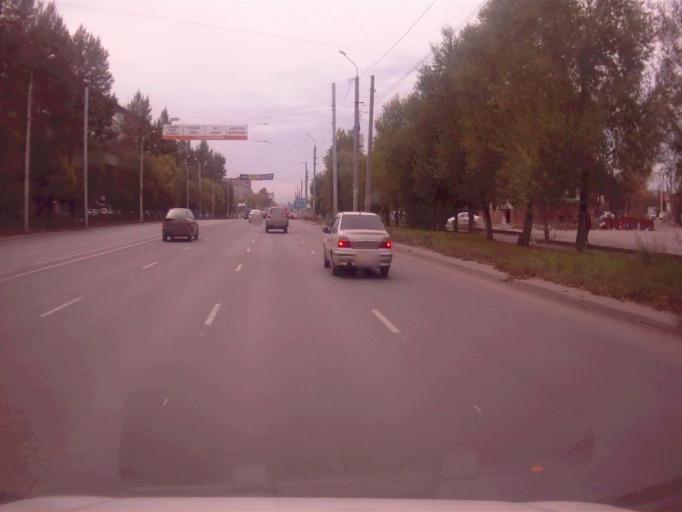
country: RU
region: Chelyabinsk
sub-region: Gorod Chelyabinsk
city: Chelyabinsk
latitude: 55.1787
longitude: 61.3637
